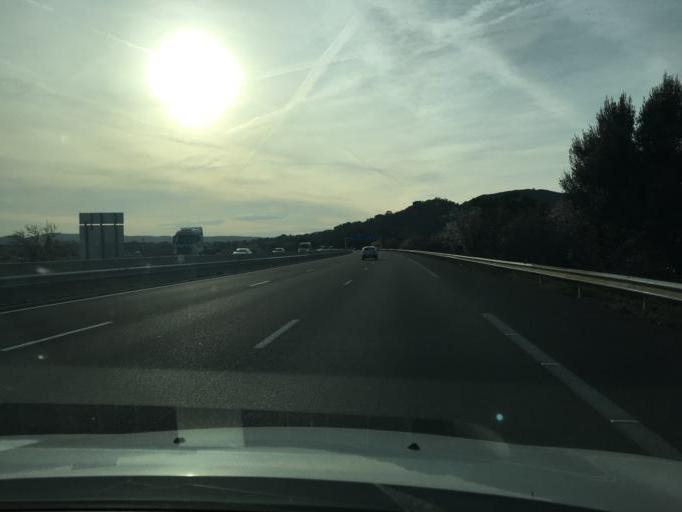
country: FR
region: Provence-Alpes-Cote d'Azur
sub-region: Departement du Var
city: Le Cannet-des-Maures
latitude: 43.4017
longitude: 6.3701
